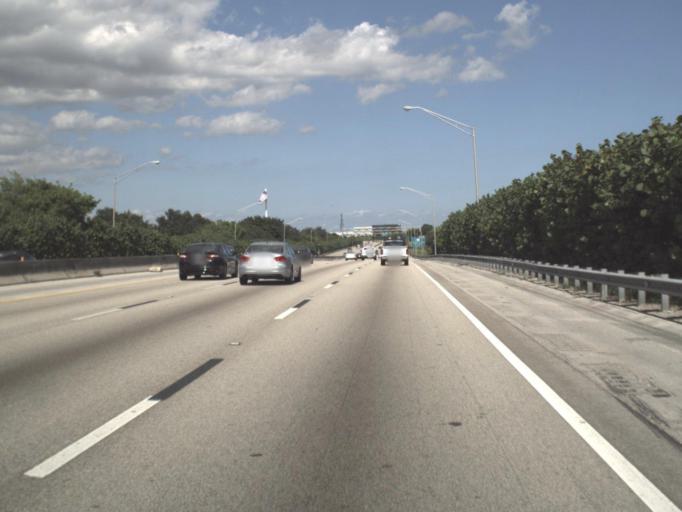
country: US
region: Florida
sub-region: Broward County
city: Pembroke Pines
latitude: 25.9955
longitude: -80.2239
